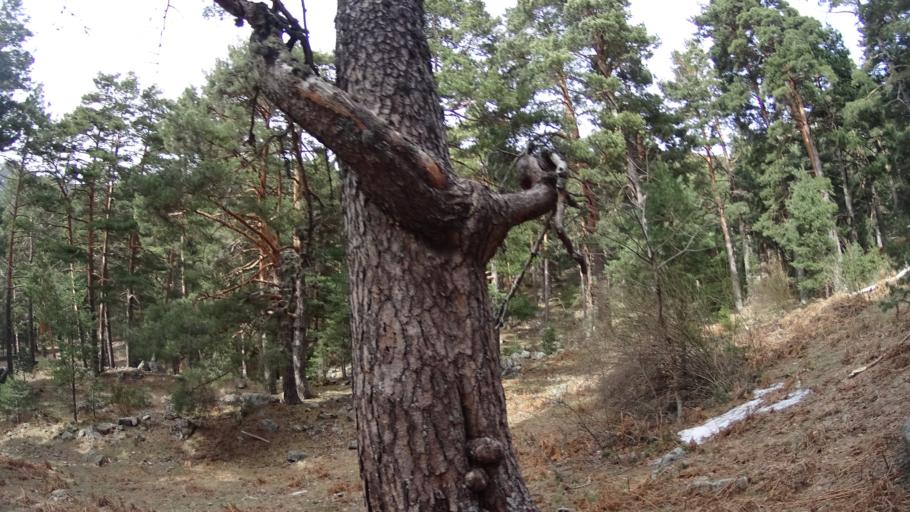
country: ES
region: Madrid
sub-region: Provincia de Madrid
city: Navacerrada
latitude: 40.7691
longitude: -3.9913
